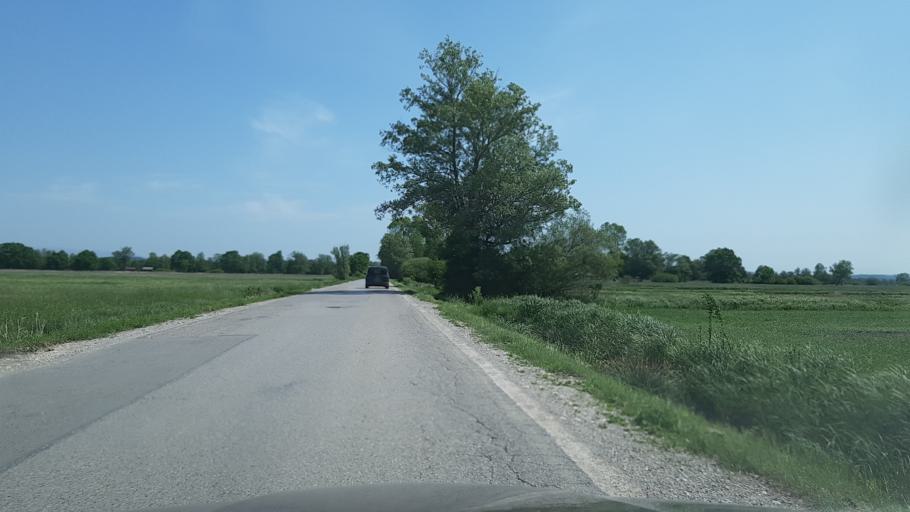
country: SI
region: Brezovica
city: Vnanje Gorice
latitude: 45.9872
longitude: 14.4445
